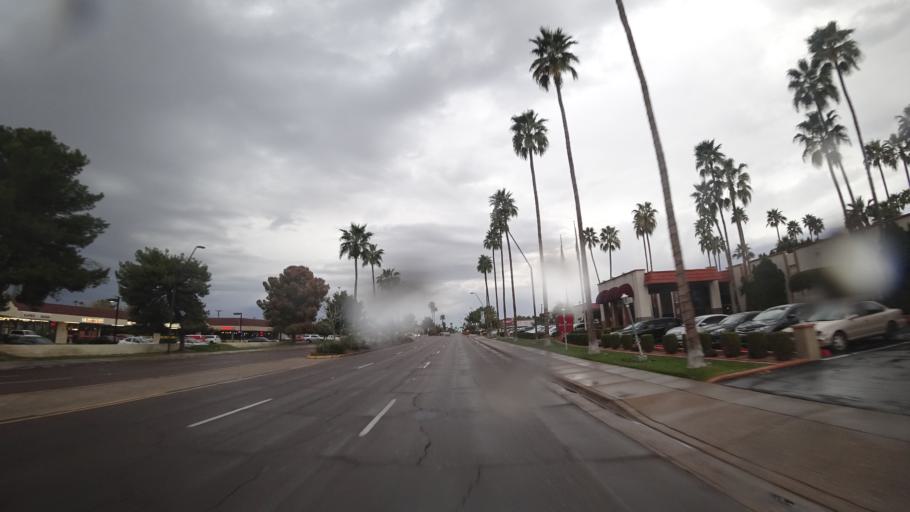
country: US
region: Arizona
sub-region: Maricopa County
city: Tempe
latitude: 33.4478
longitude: -111.9263
